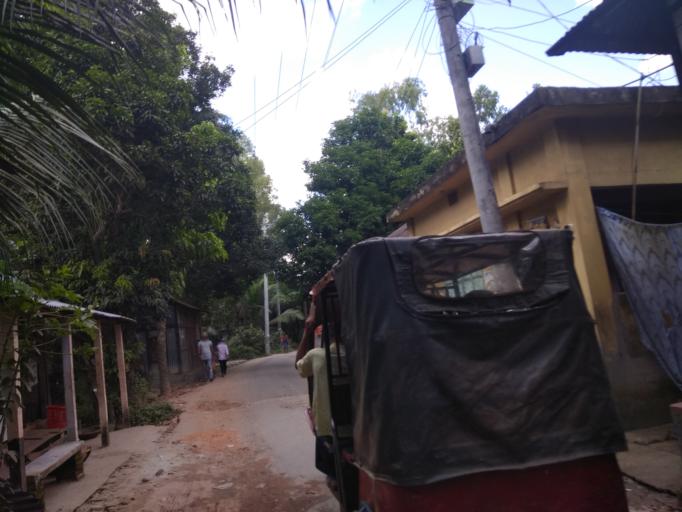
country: BD
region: Dhaka
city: Narayanganj
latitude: 23.4941
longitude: 90.4604
